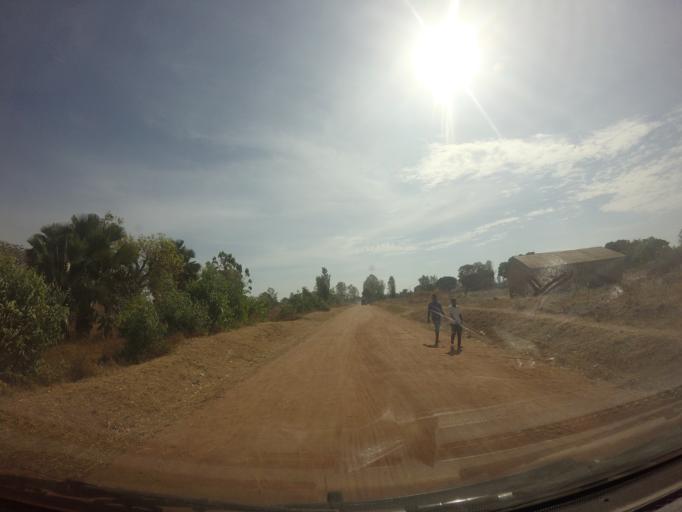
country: UG
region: Northern Region
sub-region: Maracha District
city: Maracha
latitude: 3.2685
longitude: 31.0770
